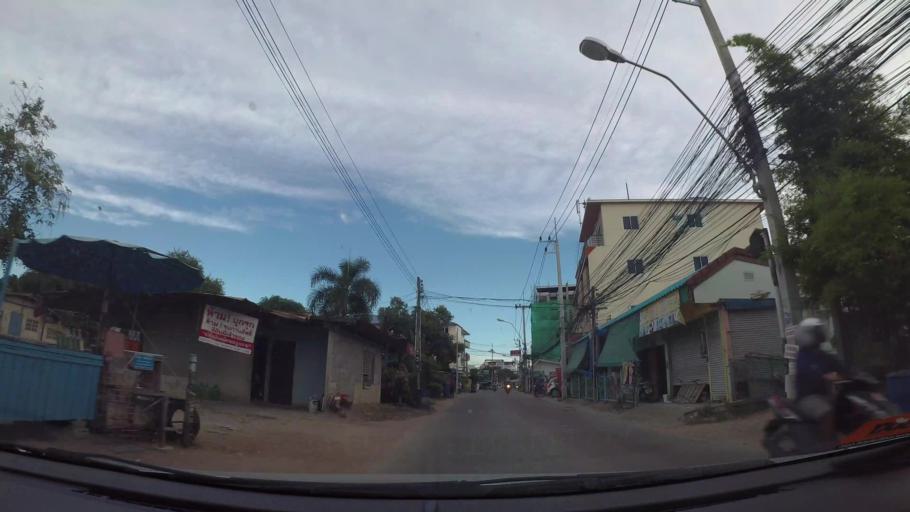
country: TH
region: Chon Buri
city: Phatthaya
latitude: 12.9119
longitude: 100.8858
